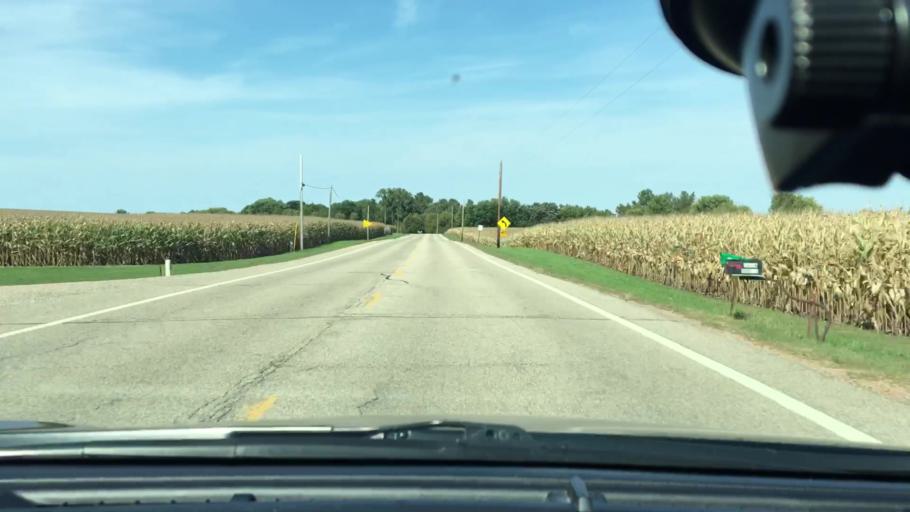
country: US
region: Minnesota
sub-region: Hennepin County
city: Corcoran
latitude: 45.1093
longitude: -93.5661
